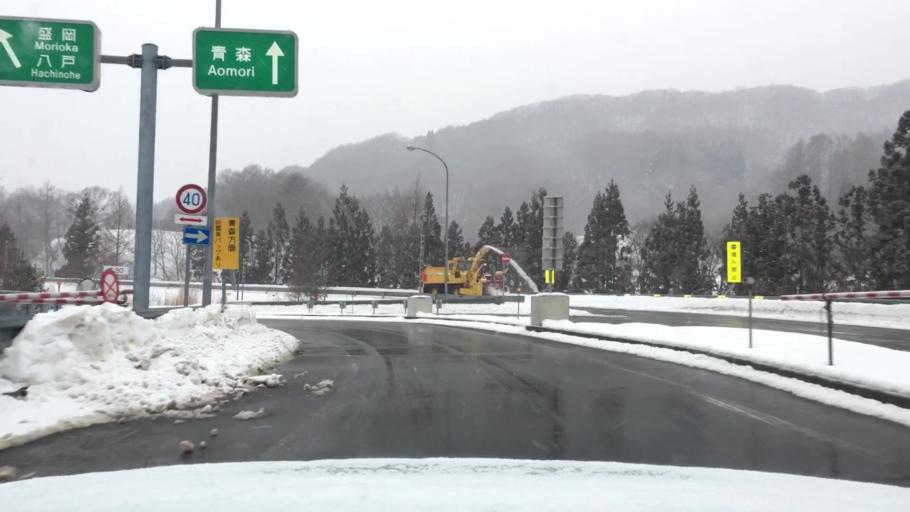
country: JP
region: Iwate
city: Ichinohe
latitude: 40.1105
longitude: 141.0495
